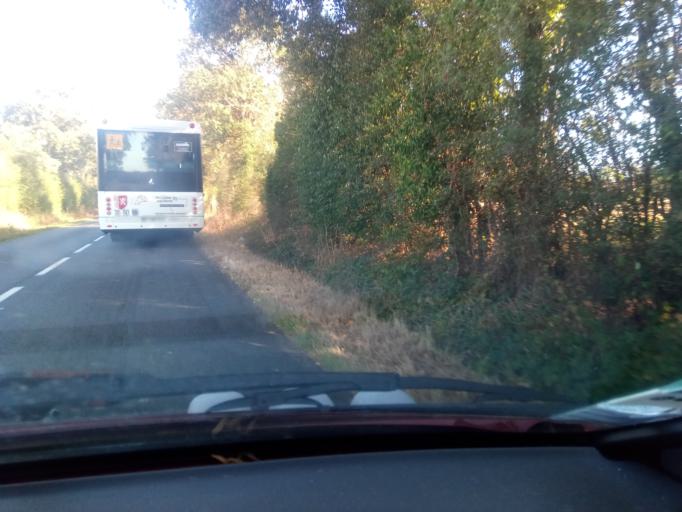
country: FR
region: Poitou-Charentes
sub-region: Departement de la Vienne
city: Availles-Limouzine
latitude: 46.1899
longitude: 0.7215
